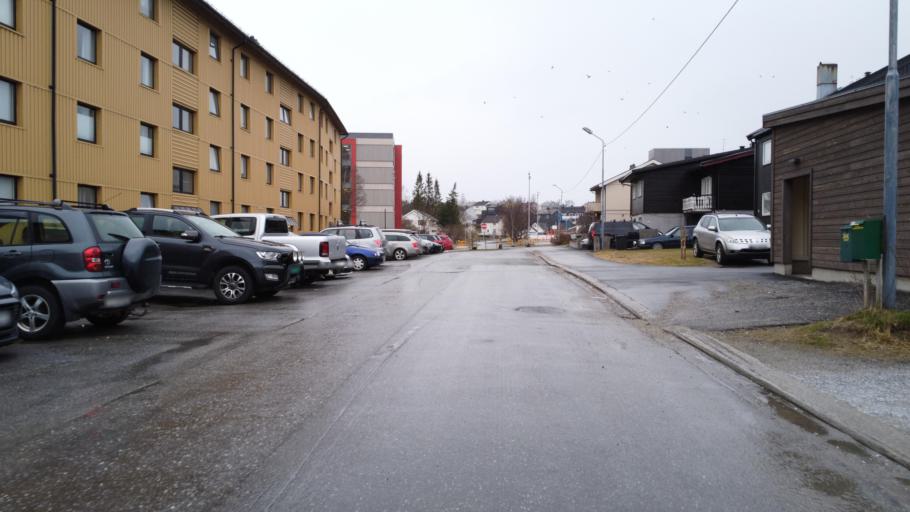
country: NO
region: Nordland
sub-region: Rana
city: Mo i Rana
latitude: 66.3108
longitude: 14.1461
